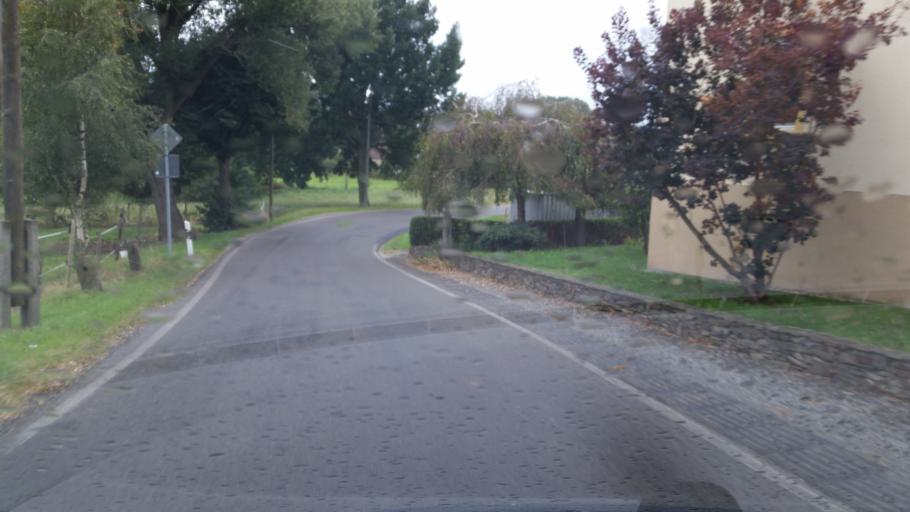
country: DE
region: Saxony
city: Haselbachtal
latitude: 51.2866
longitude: 14.0425
